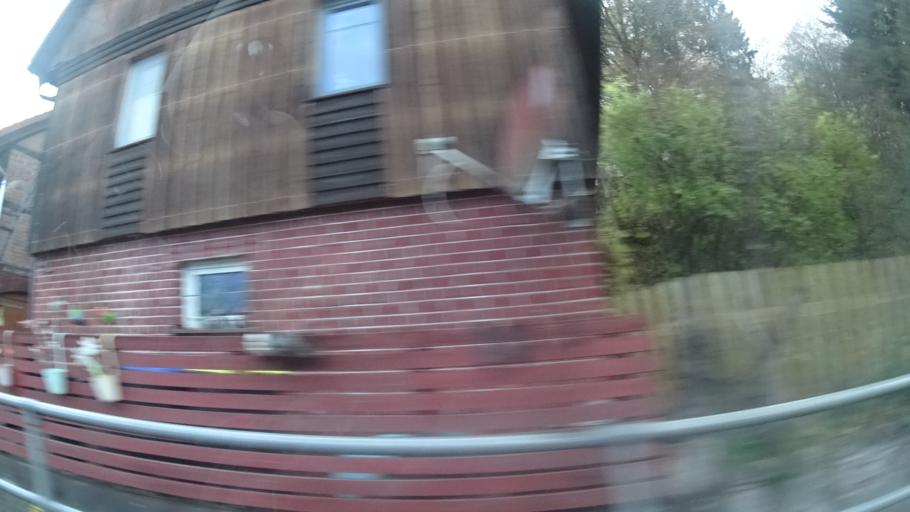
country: DE
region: Hesse
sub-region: Regierungsbezirk Kassel
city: Eichenzell
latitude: 50.5106
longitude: 9.6660
